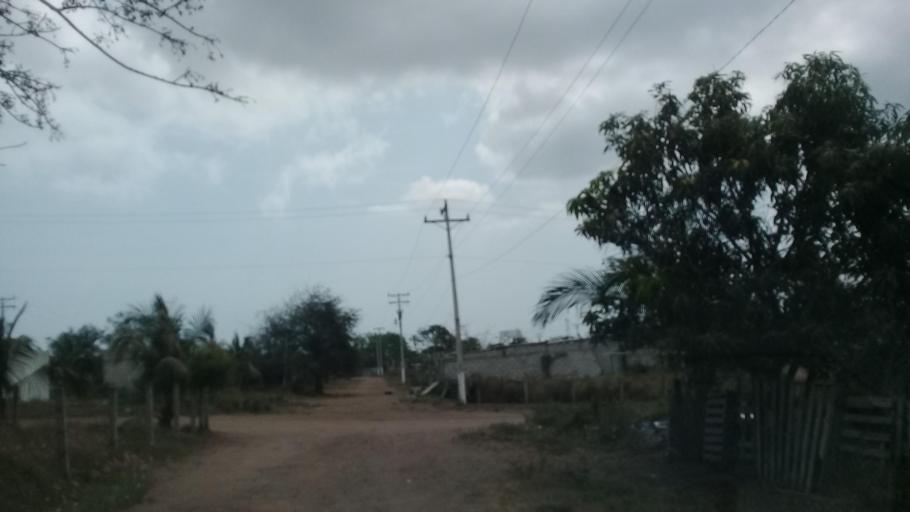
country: MX
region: Veracruz
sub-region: Veracruz
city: Las Amapolas
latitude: 19.1345
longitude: -96.2423
